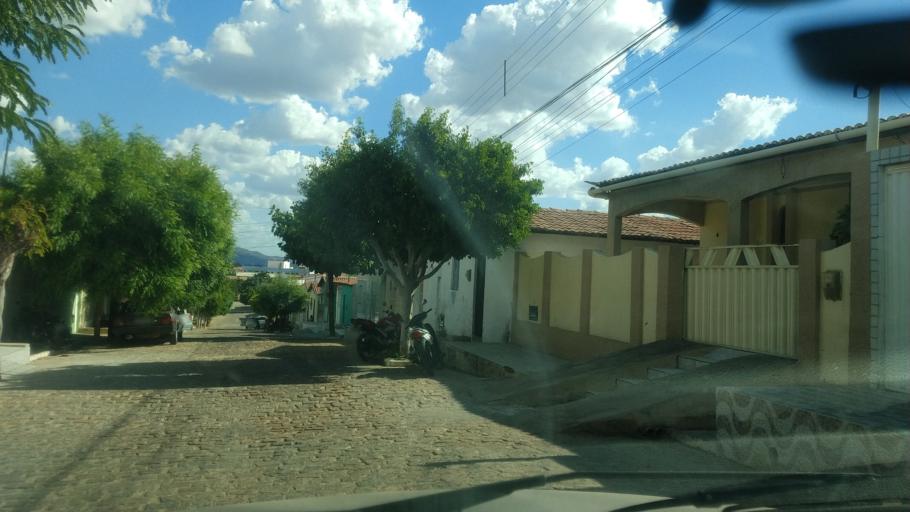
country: BR
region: Rio Grande do Norte
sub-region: Currais Novos
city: Currais Novos
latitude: -6.2188
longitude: -36.6815
